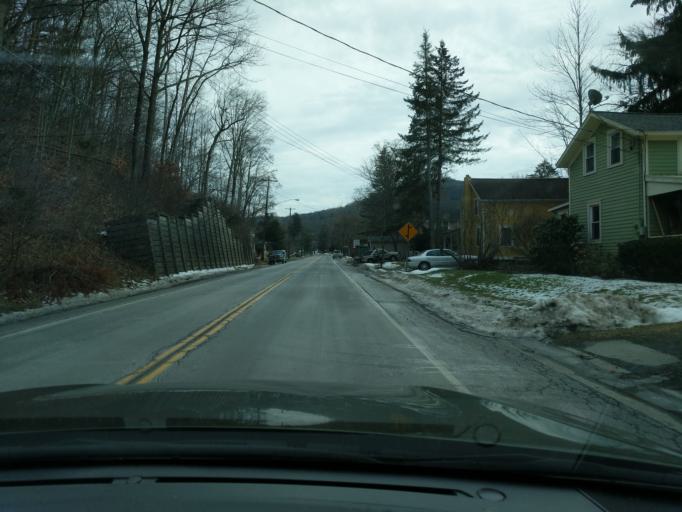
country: US
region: New York
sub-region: Tompkins County
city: East Ithaca
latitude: 42.3823
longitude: -76.3991
